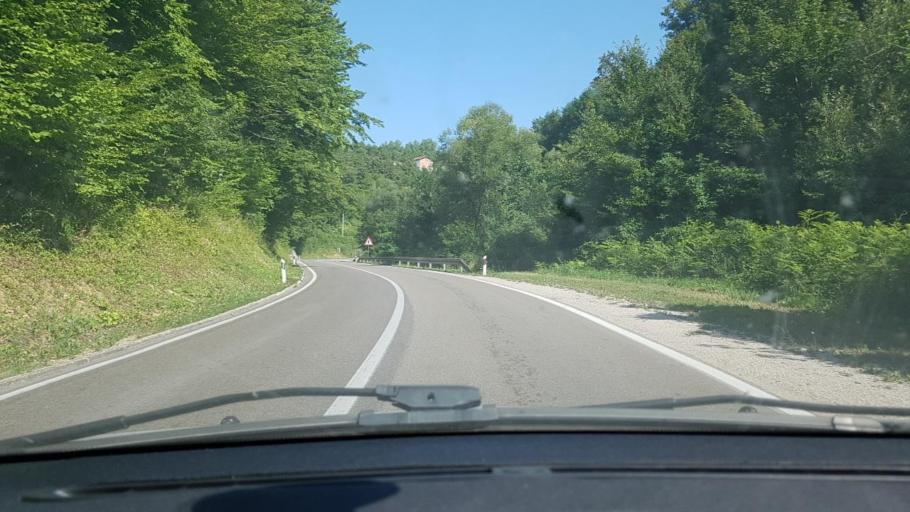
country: BA
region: Federation of Bosnia and Herzegovina
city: Skokovi
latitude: 45.0103
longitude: 15.9045
